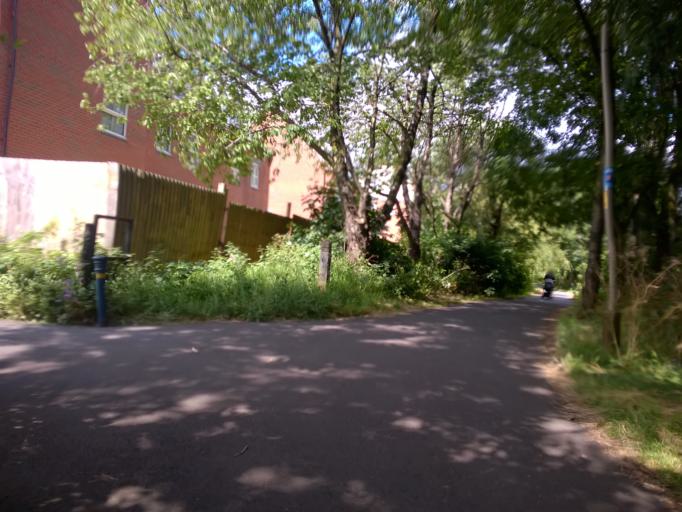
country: GB
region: England
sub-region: City of Leicester
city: Leicester
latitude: 52.6512
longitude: -1.1335
